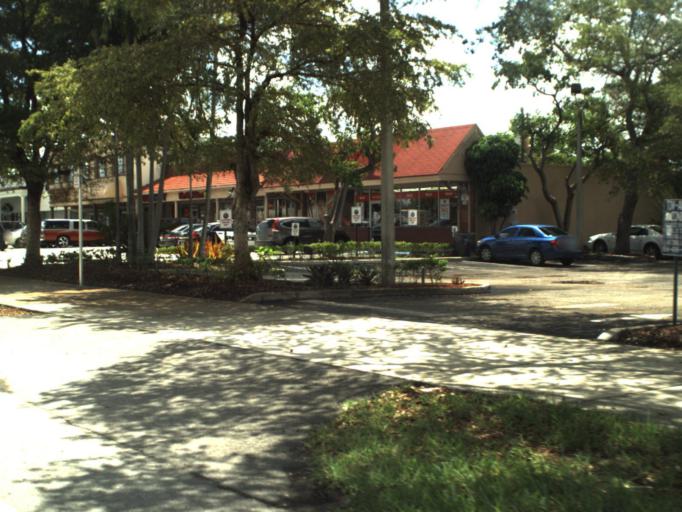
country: US
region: Florida
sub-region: Broward County
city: Carver Ranches
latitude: 26.0104
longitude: -80.1872
